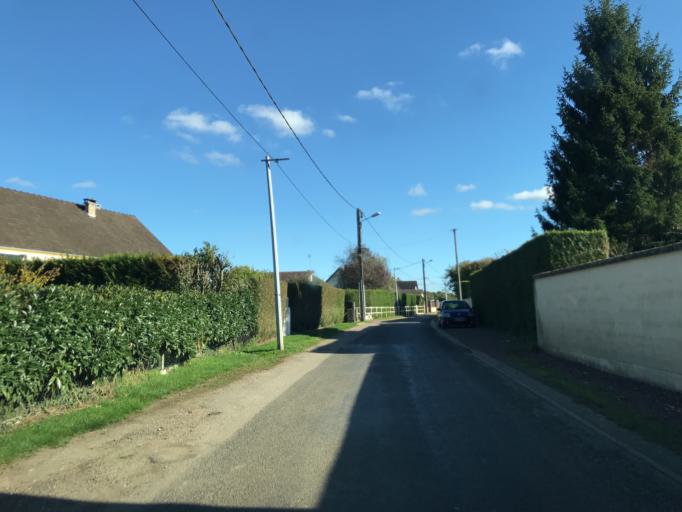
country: FR
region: Haute-Normandie
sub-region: Departement de l'Eure
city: Gravigny
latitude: 49.0827
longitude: 1.2371
